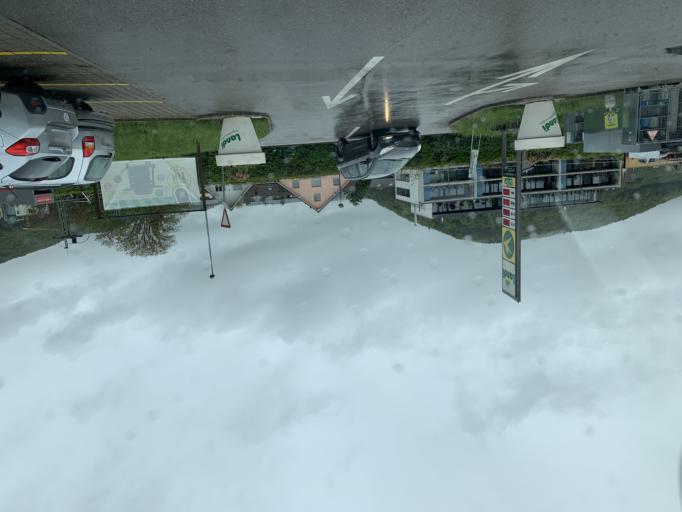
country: CH
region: Schaffhausen
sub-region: Bezirk Schaffhausen
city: Beringen
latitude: 47.6943
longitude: 8.5719
